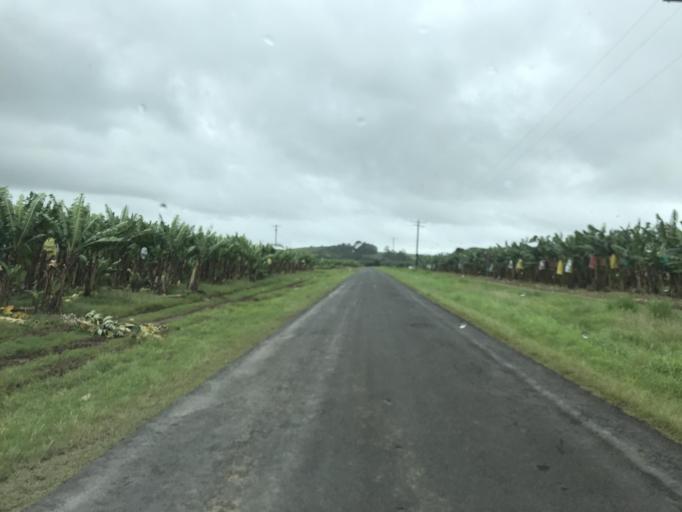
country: AU
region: Queensland
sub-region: Cassowary Coast
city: Innisfail
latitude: -17.5094
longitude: 145.9788
